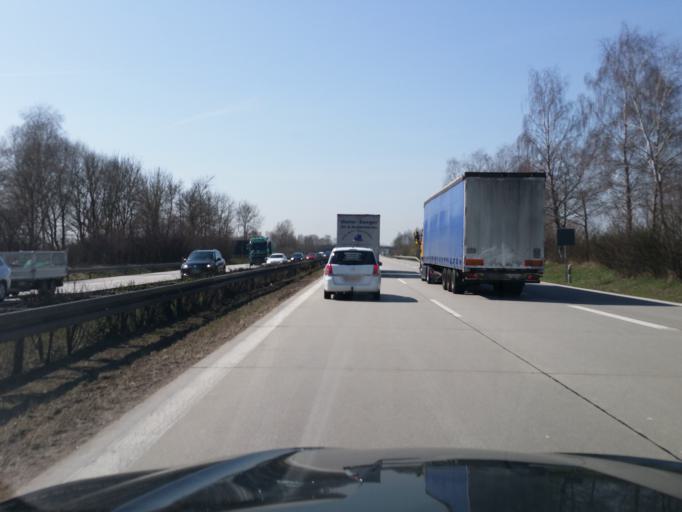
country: DE
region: Bavaria
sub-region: Upper Bavaria
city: Langenpreising
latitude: 48.4360
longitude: 11.9505
